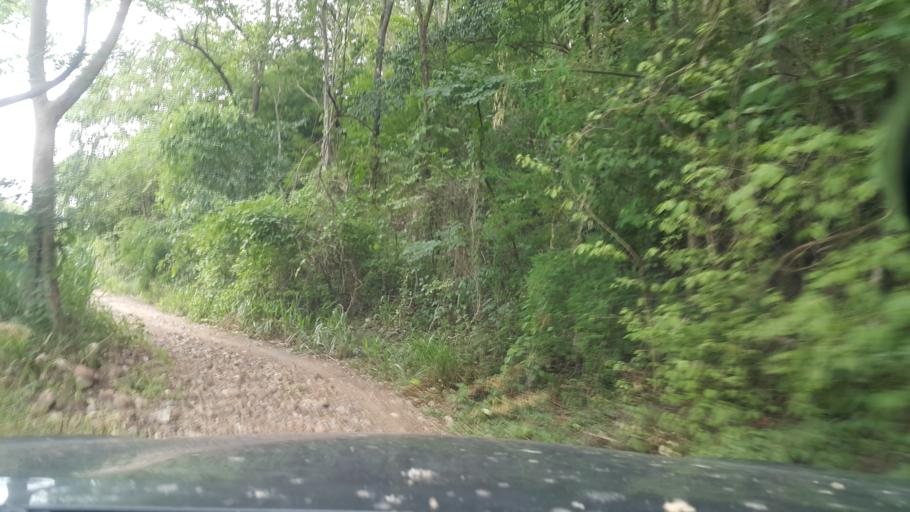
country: TH
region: Chiang Mai
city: Hang Dong
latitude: 18.6844
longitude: 98.8415
